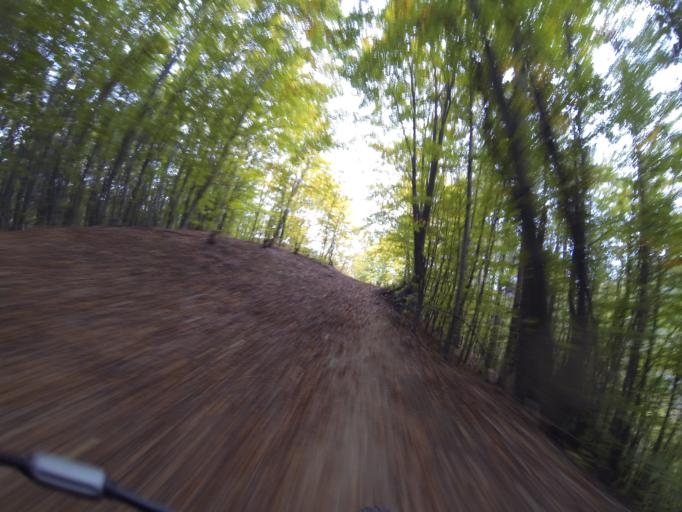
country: RO
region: Gorj
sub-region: Comuna Tismana
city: Sohodol
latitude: 45.0842
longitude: 22.8850
